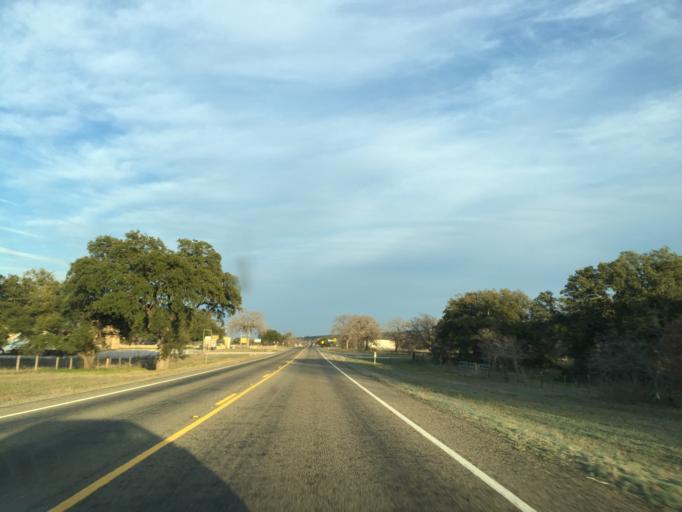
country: US
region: Texas
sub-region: Llano County
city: Buchanan Dam
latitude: 30.7331
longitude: -98.4747
